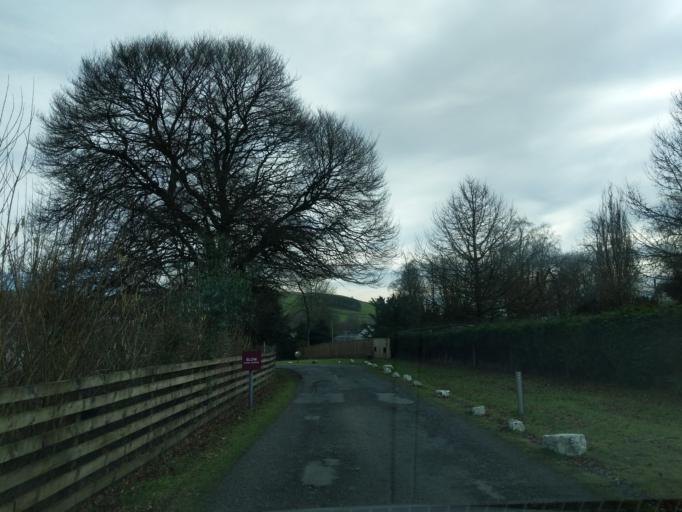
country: GB
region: Scotland
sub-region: The Scottish Borders
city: Peebles
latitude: 55.7126
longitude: -3.2097
